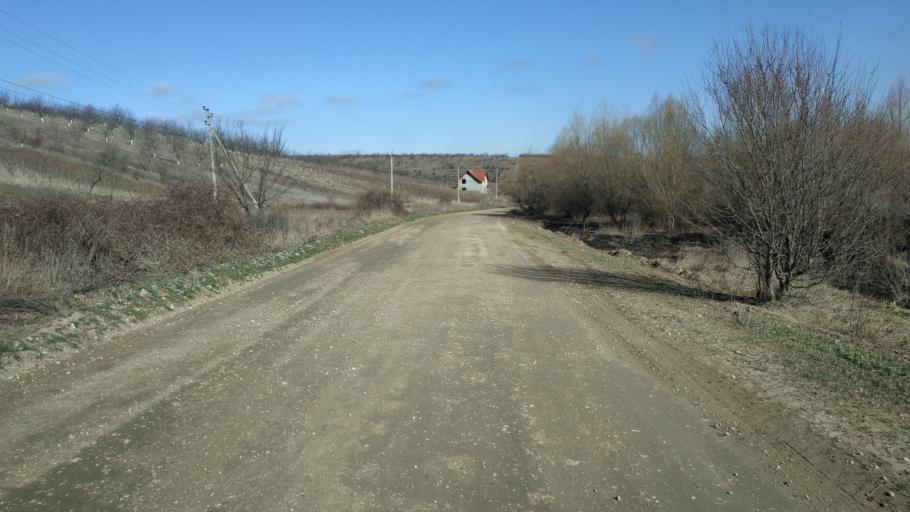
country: MD
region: Hincesti
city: Hincesti
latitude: 46.9255
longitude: 28.6291
